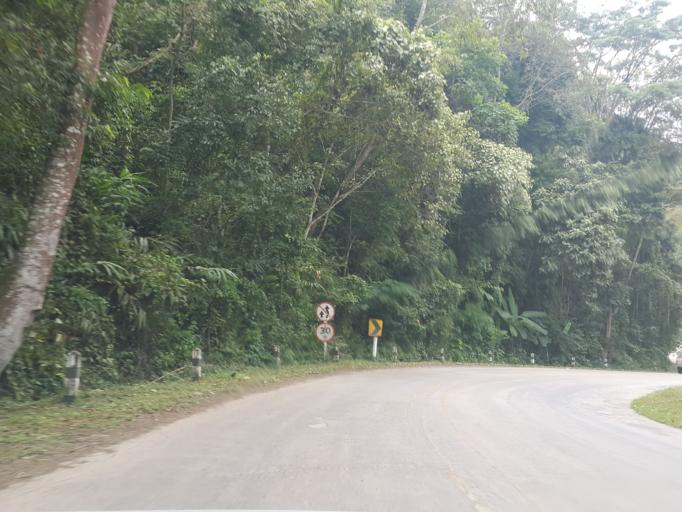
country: TH
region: Chiang Mai
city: Mae Taeng
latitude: 19.1225
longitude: 98.7369
